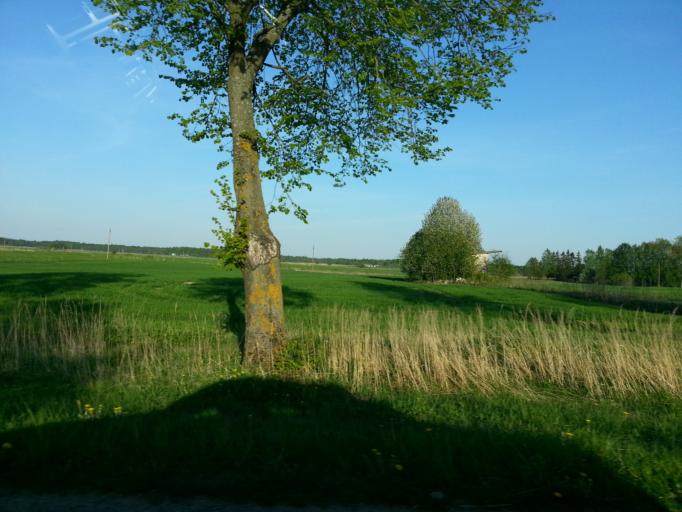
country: LT
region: Vilnius County
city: Ukmerge
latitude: 55.4204
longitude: 24.5838
